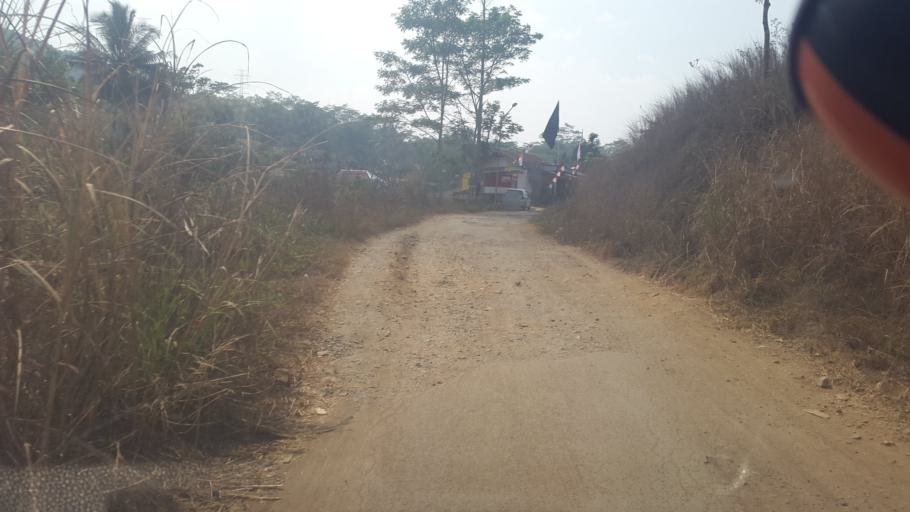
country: ID
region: West Java
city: Pasirlaja
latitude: -7.0531
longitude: 106.8644
